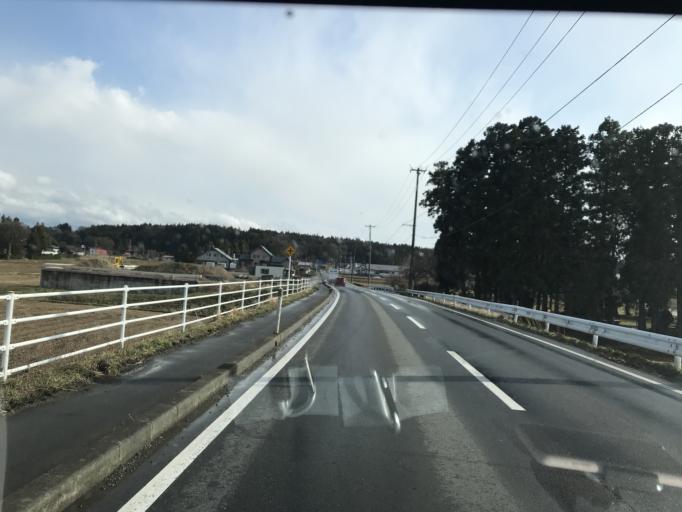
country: JP
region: Iwate
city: Kitakami
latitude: 39.2868
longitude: 141.0556
